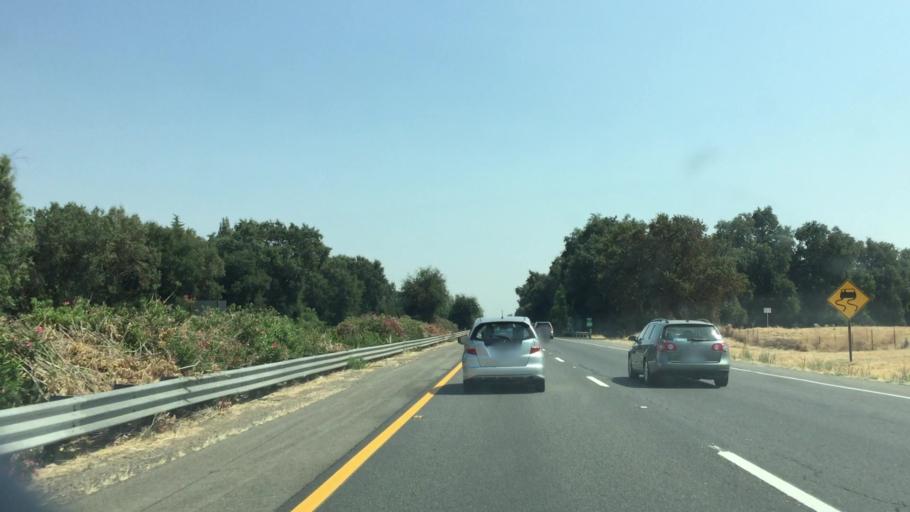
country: US
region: California
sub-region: Sacramento County
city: Galt
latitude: 38.2468
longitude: -121.2889
